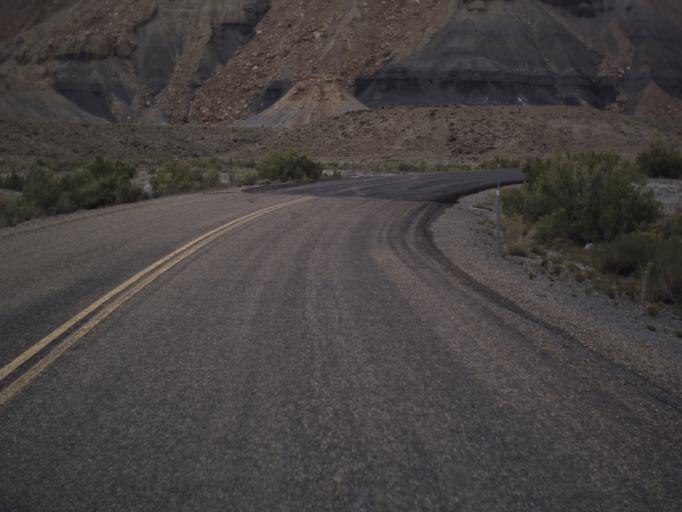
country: US
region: Utah
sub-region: Emery County
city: Ferron
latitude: 38.8145
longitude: -111.2111
